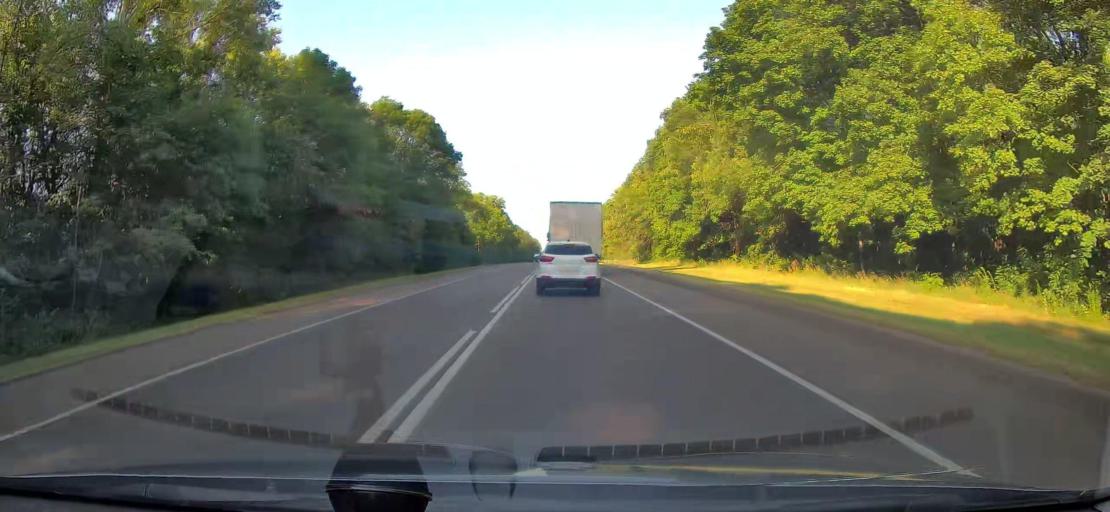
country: RU
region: Tula
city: Chern'
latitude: 53.4785
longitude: 36.9838
